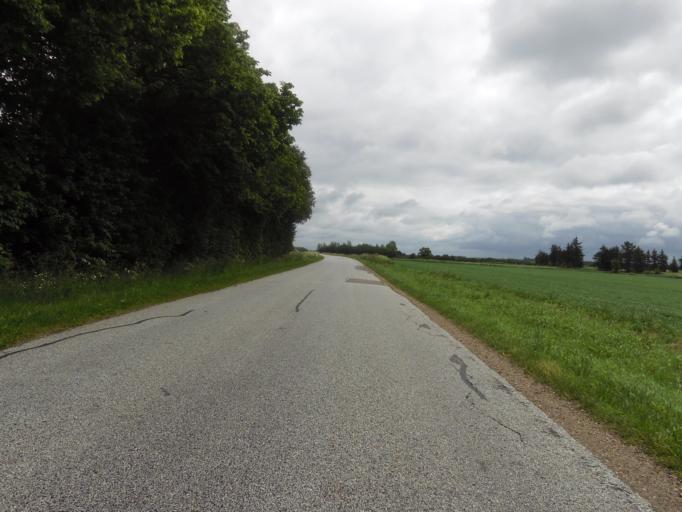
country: DK
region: South Denmark
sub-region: Haderslev Kommune
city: Gram
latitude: 55.2616
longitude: 9.0688
